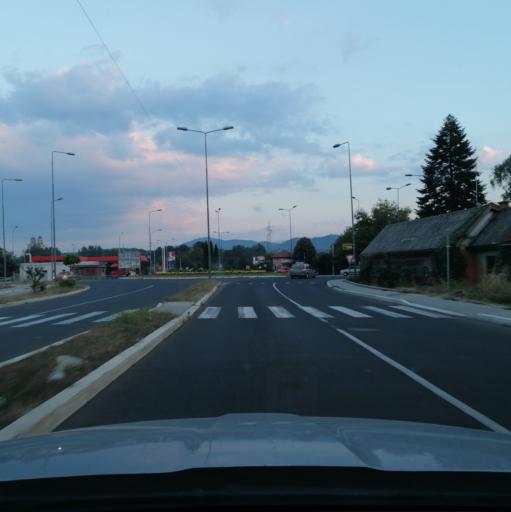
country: RS
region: Central Serbia
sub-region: Raski Okrug
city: Kraljevo
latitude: 43.7132
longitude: 20.6940
